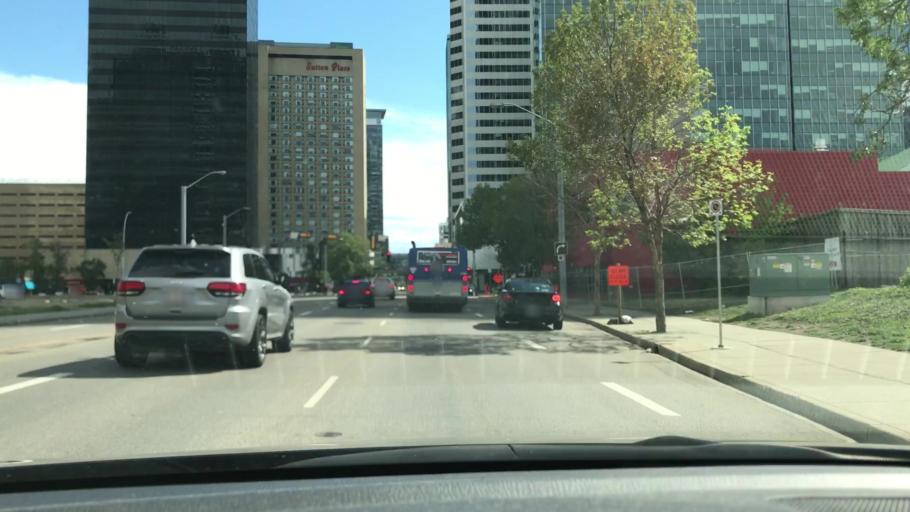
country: CA
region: Alberta
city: Edmonton
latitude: 53.5472
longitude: -113.4938
